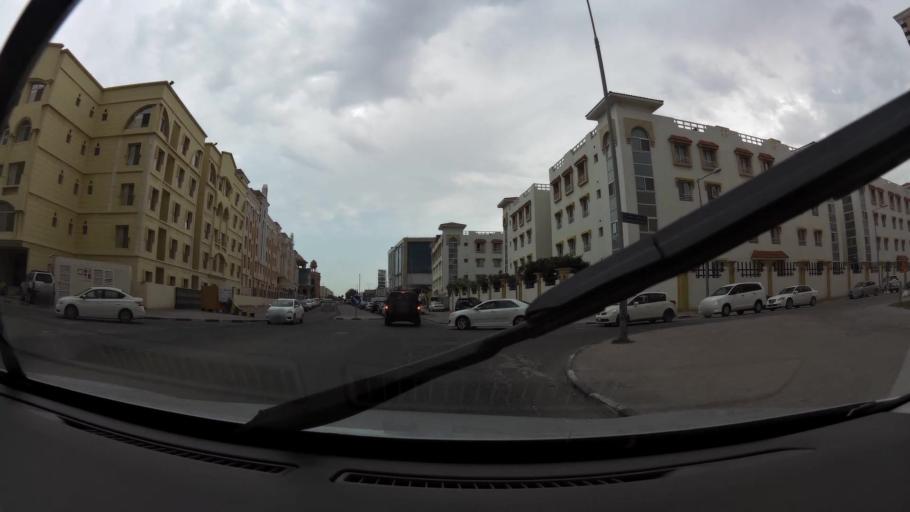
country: QA
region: Baladiyat ad Dawhah
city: Doha
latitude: 25.2755
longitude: 51.4978
